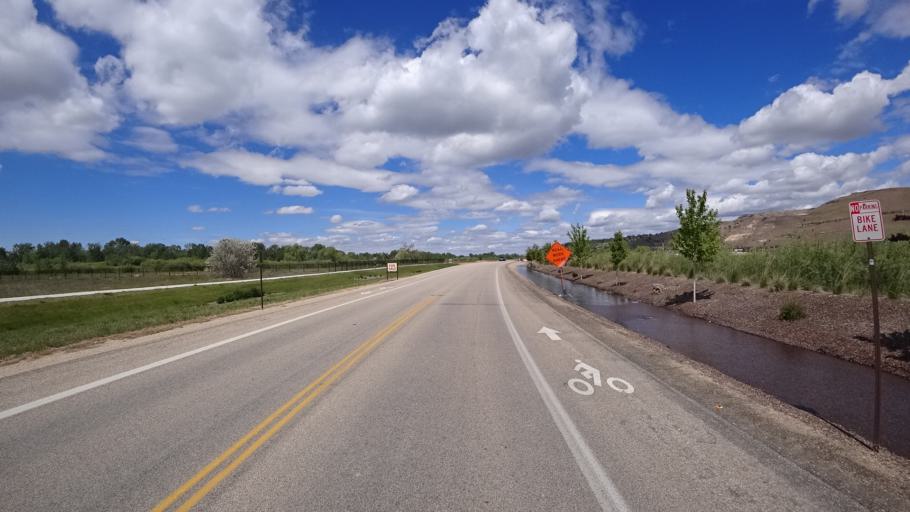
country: US
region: Idaho
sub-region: Ada County
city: Boise
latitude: 43.5694
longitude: -116.1308
